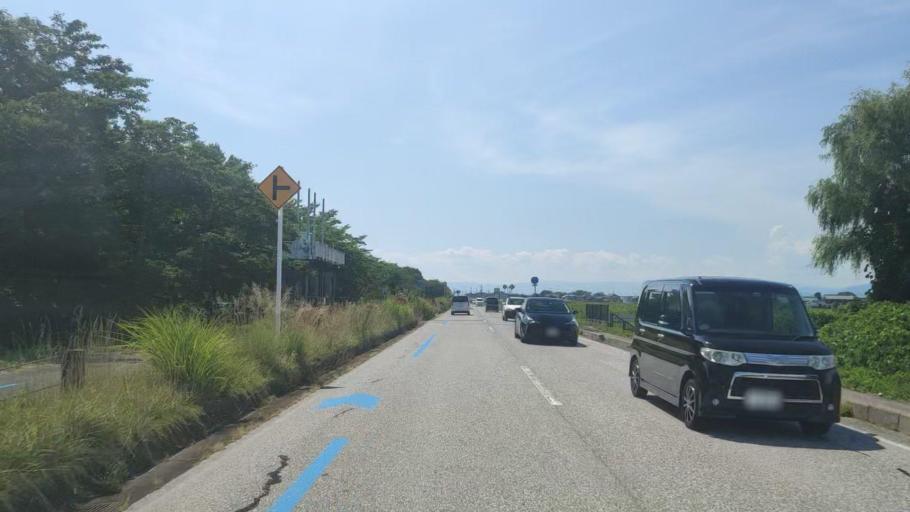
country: JP
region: Shiga Prefecture
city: Nagahama
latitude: 35.3883
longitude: 136.2297
